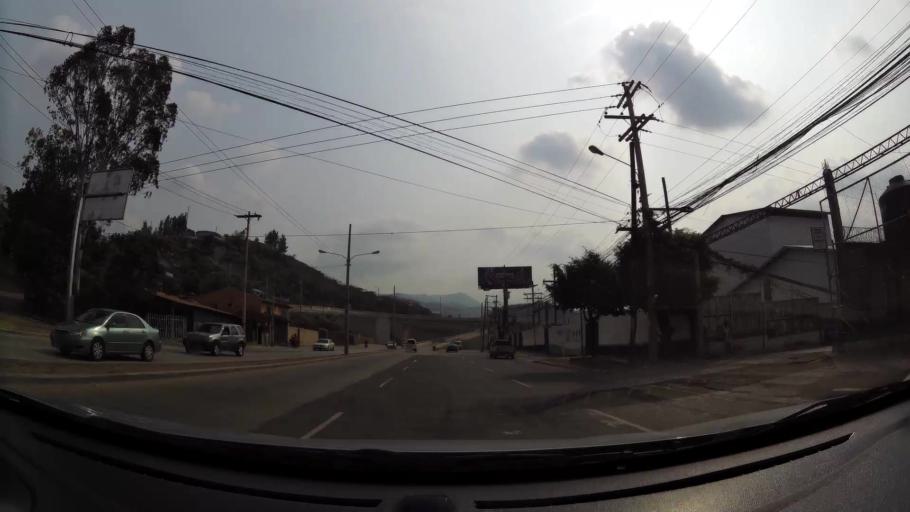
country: HN
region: Francisco Morazan
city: Tegucigalpa
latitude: 14.1070
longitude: -87.1709
